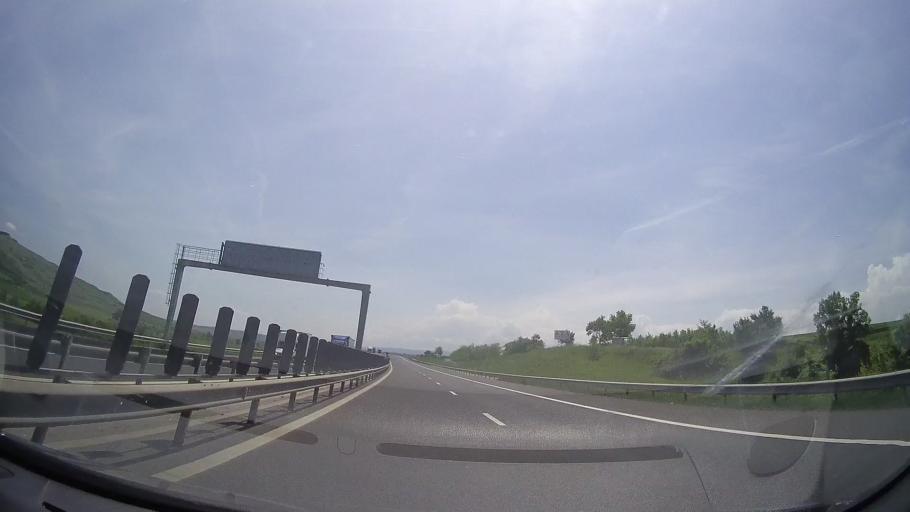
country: RO
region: Alba
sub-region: Municipiul Sebes
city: Sebes
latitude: 45.9405
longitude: 23.5959
